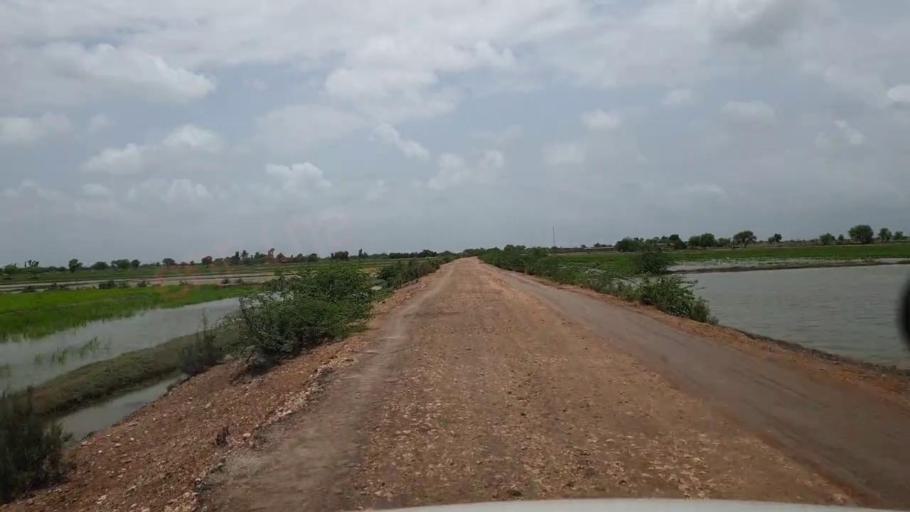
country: PK
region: Sindh
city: Kario
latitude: 24.7200
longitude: 68.5727
